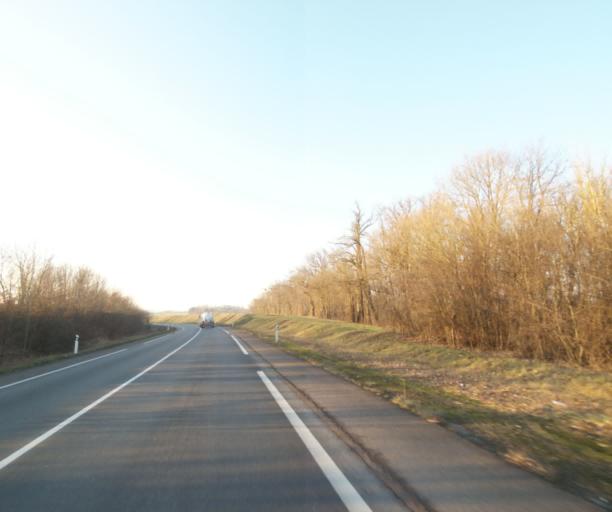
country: FR
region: Champagne-Ardenne
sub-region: Departement de la Haute-Marne
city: Bienville
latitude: 48.5447
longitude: 5.0786
